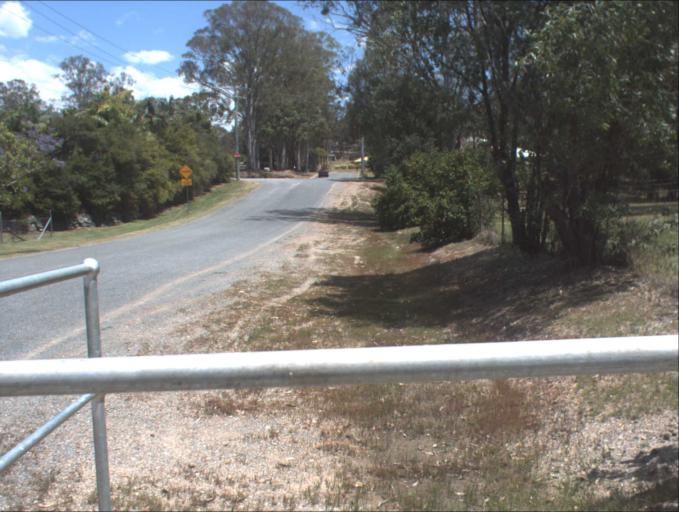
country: AU
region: Queensland
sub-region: Logan
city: Windaroo
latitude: -27.7408
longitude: 153.1855
